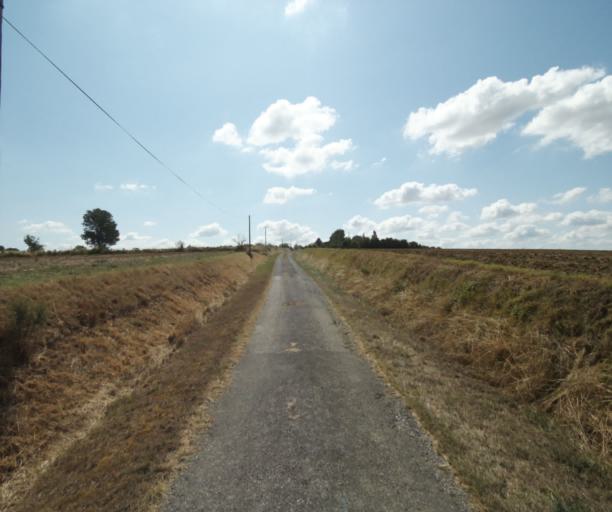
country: FR
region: Midi-Pyrenees
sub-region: Departement de la Haute-Garonne
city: Auriac-sur-Vendinelle
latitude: 43.4520
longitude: 1.7847
